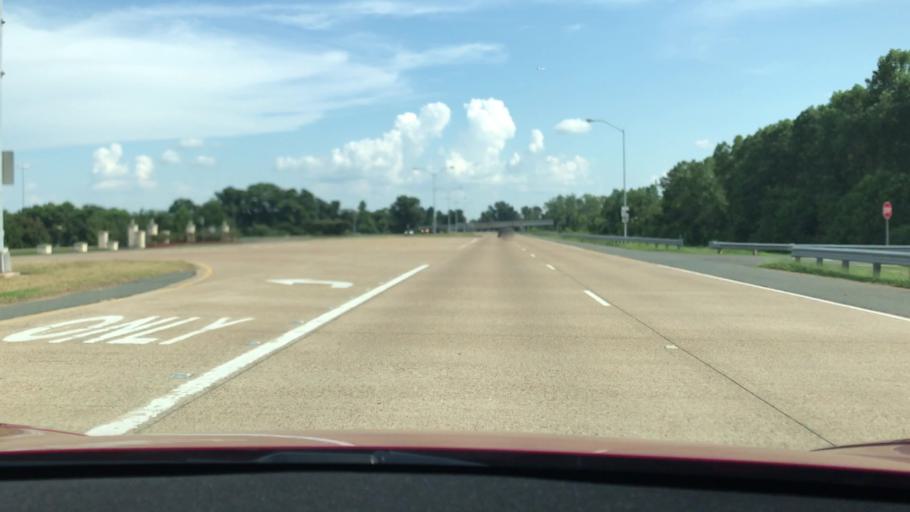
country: US
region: Louisiana
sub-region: Bossier Parish
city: Bossier City
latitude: 32.4656
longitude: -93.6775
